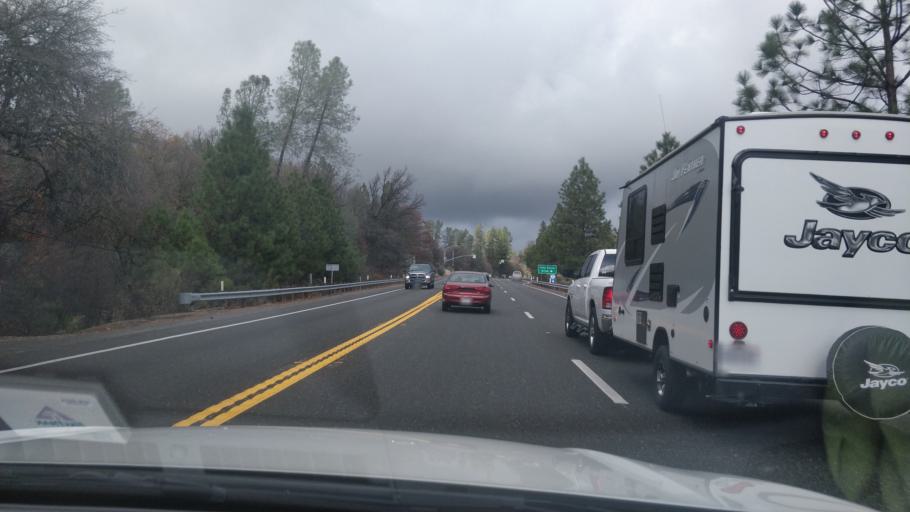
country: US
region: California
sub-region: Nevada County
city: Alta Sierra
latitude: 39.1389
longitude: -121.0716
